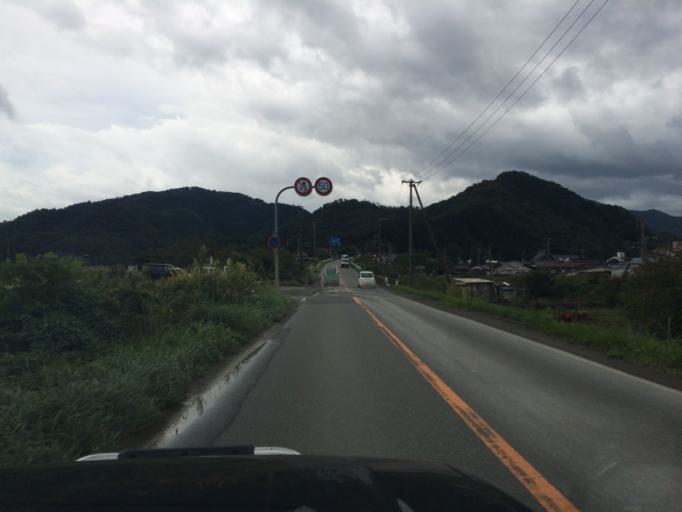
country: JP
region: Hyogo
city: Toyooka
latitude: 35.4083
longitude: 134.7784
